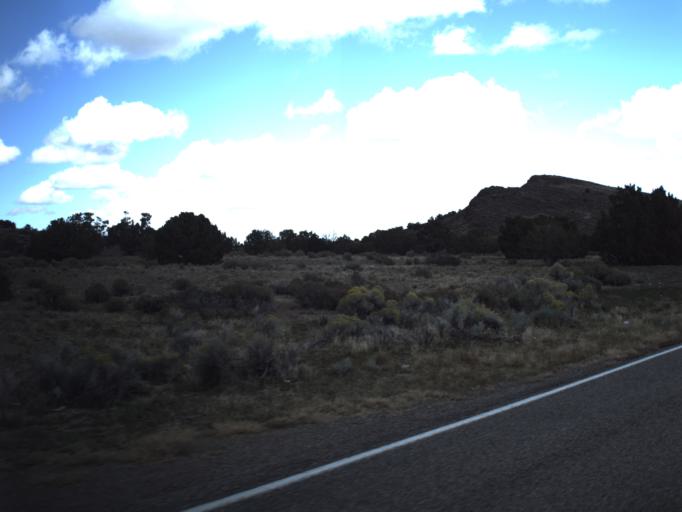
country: US
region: Utah
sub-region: Beaver County
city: Milford
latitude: 38.4613
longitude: -113.2490
